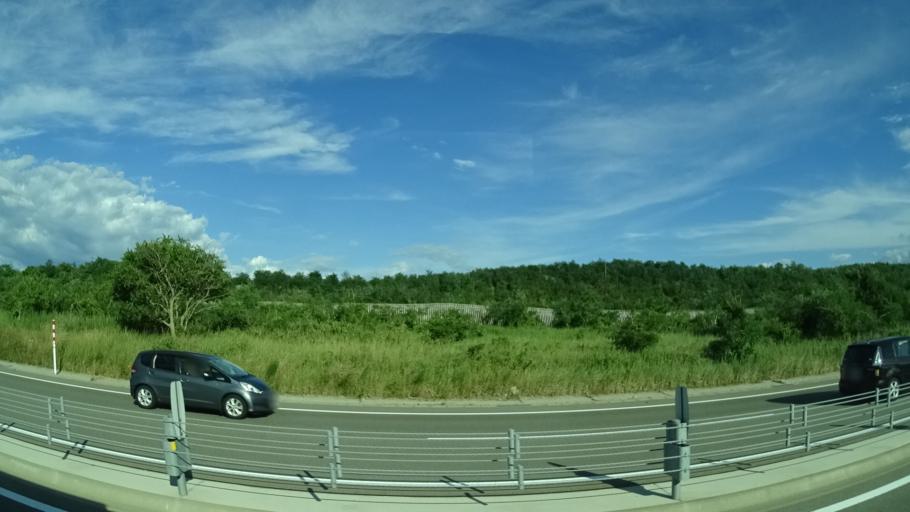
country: JP
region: Ishikawa
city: Tsubata
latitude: 36.7114
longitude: 136.6793
